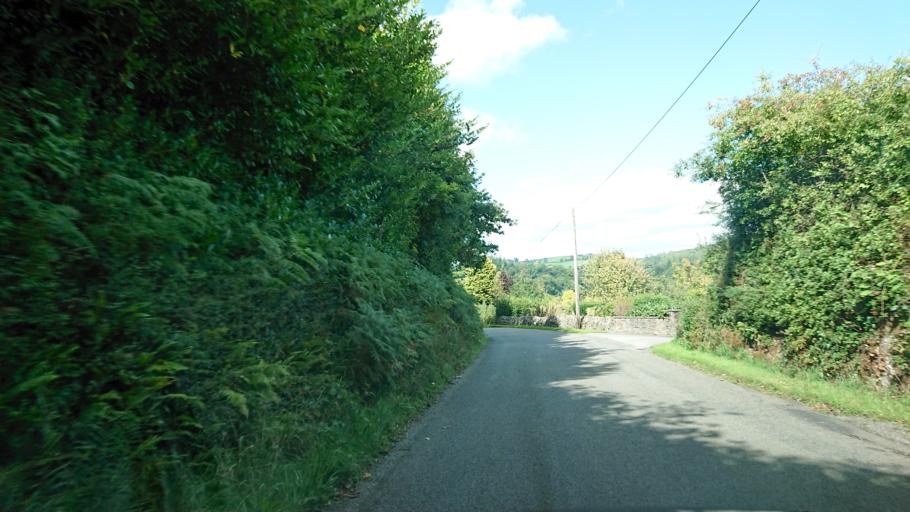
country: IE
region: Munster
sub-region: Waterford
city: Dungarvan
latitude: 52.1200
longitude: -7.6874
